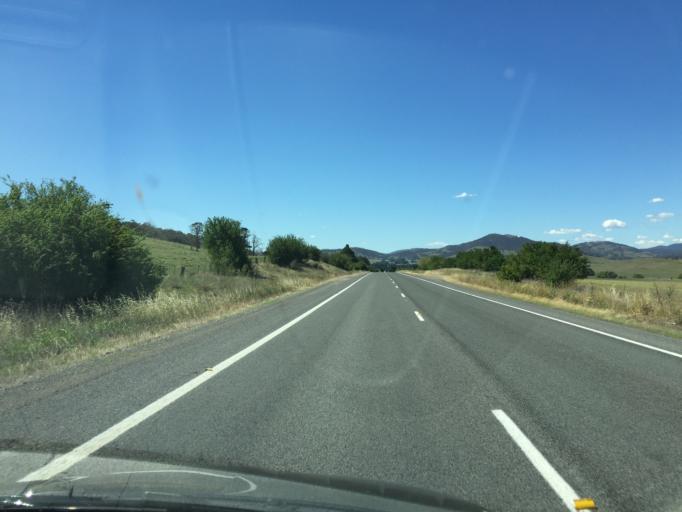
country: AU
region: Australian Capital Territory
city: Macarthur
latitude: -35.7391
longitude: 149.1606
